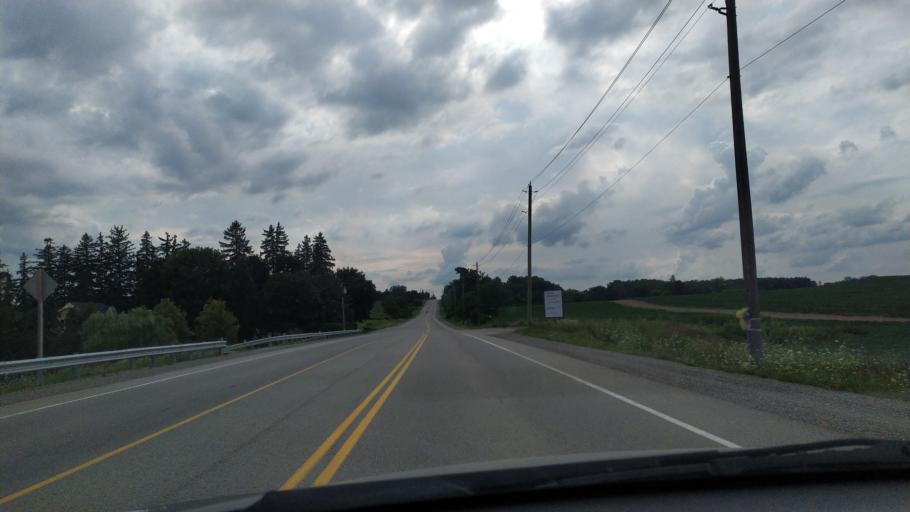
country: CA
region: Ontario
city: Kitchener
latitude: 43.3649
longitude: -80.4419
